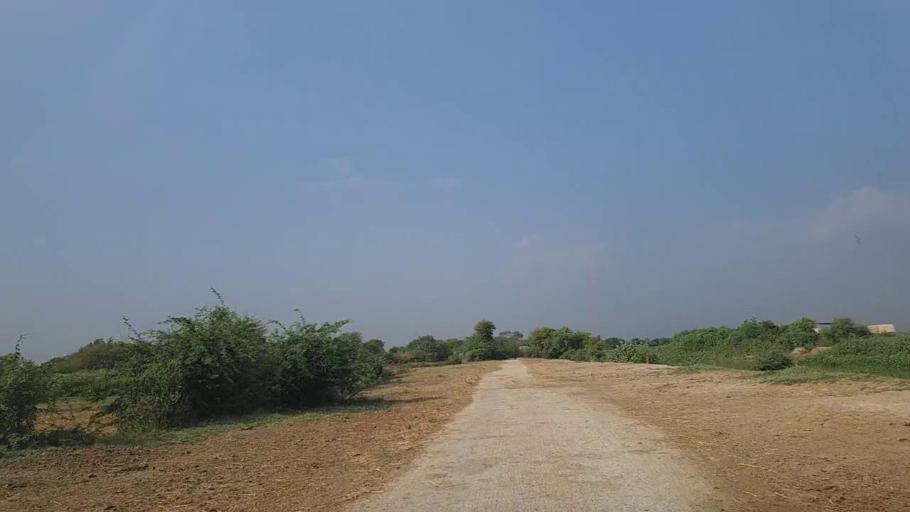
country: PK
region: Sindh
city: Daro Mehar
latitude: 24.7252
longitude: 68.1560
